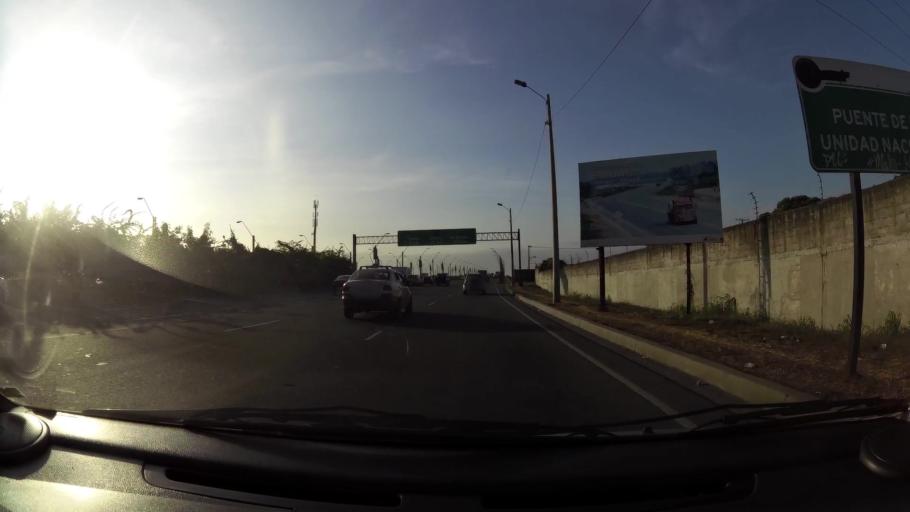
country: EC
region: Guayas
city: Eloy Alfaro
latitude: -2.1537
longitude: -79.8626
